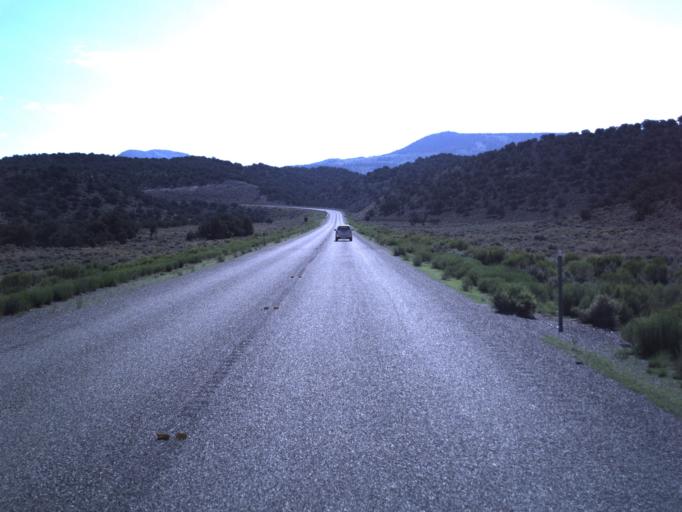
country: US
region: Utah
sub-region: Wayne County
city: Loa
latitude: 38.4792
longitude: -111.5613
